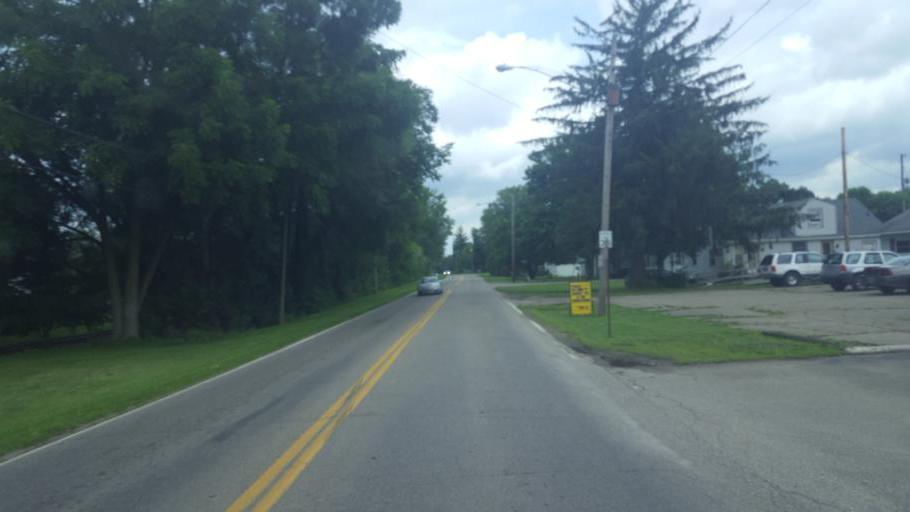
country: US
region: Ohio
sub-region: Knox County
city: Mount Vernon
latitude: 40.3756
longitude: -82.4872
